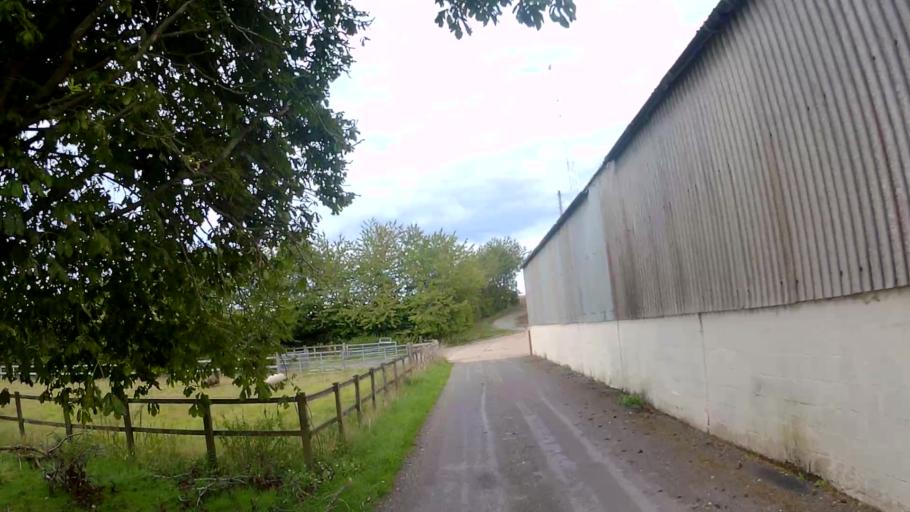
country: GB
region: England
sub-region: Hampshire
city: Kings Worthy
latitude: 51.1451
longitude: -1.2164
